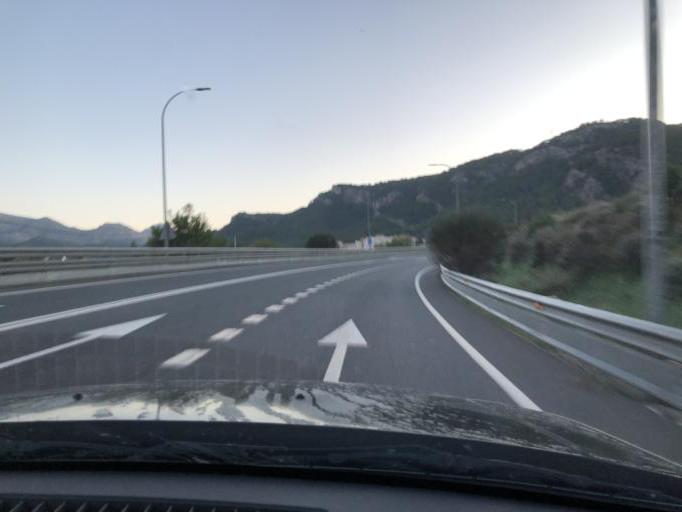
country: ES
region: Balearic Islands
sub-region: Illes Balears
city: Andratx
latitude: 39.5668
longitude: 2.4199
